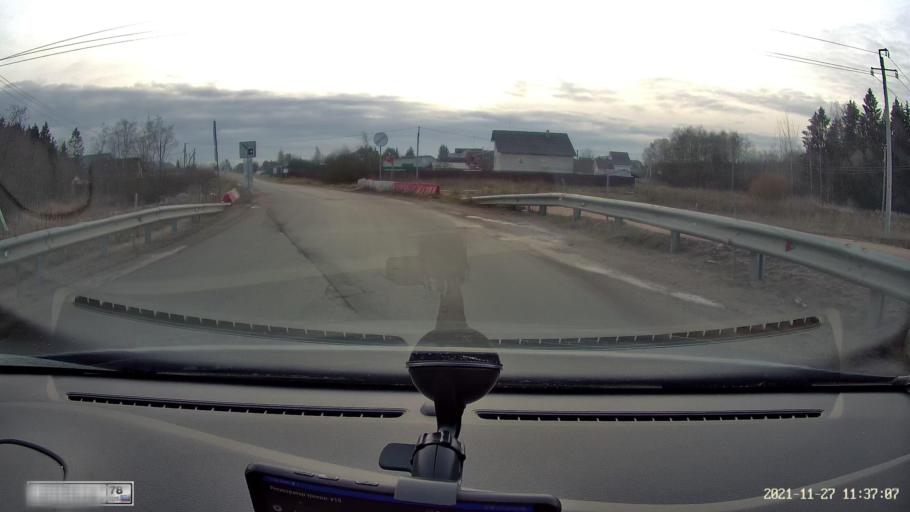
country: RU
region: Leningrad
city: Russko-Vysotskoye
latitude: 59.6957
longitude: 29.9836
